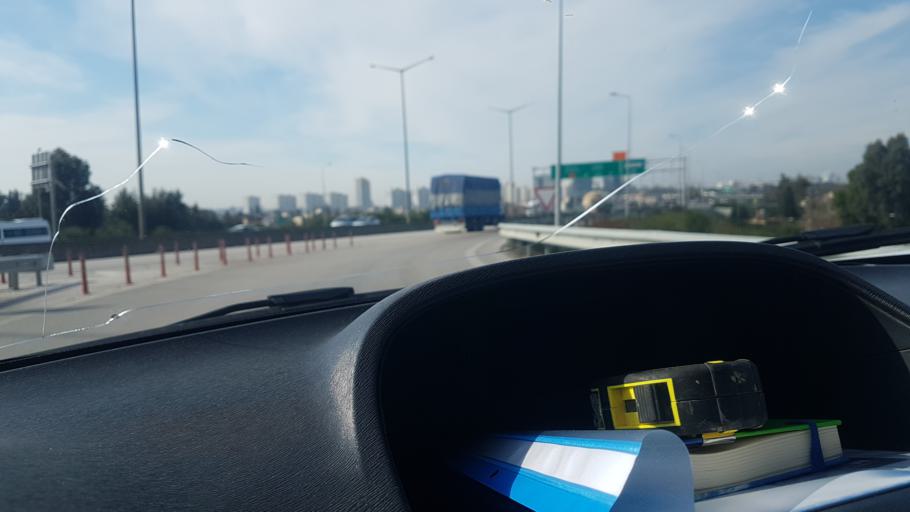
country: TR
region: Adana
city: Adana
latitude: 37.0253
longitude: 35.3454
